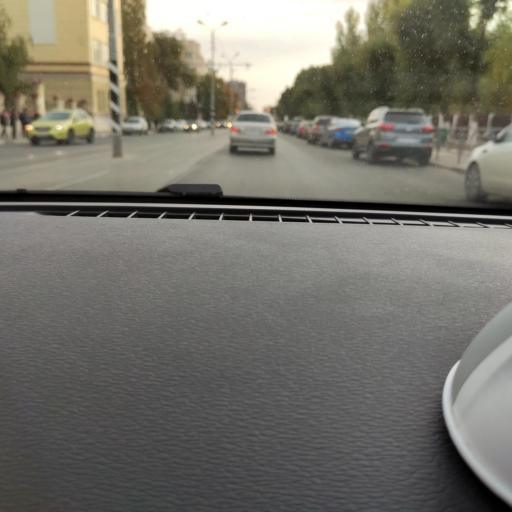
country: RU
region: Samara
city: Samara
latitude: 53.2003
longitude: 50.1111
